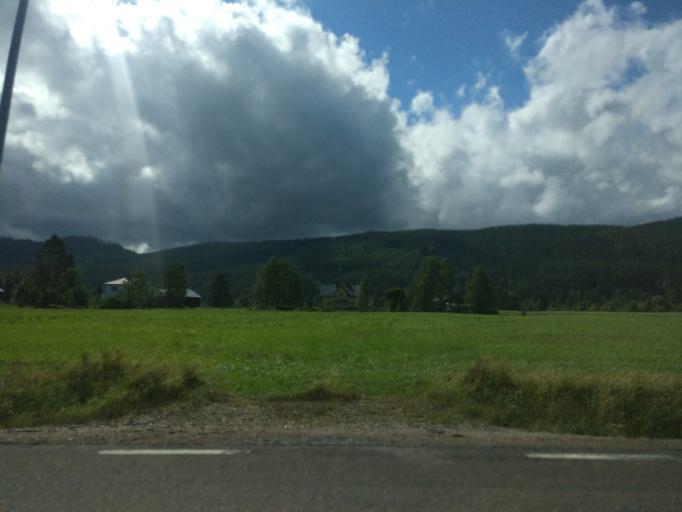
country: SE
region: Vaermland
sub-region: Hagfors Kommun
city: Ekshaerad
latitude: 60.3545
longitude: 13.3297
